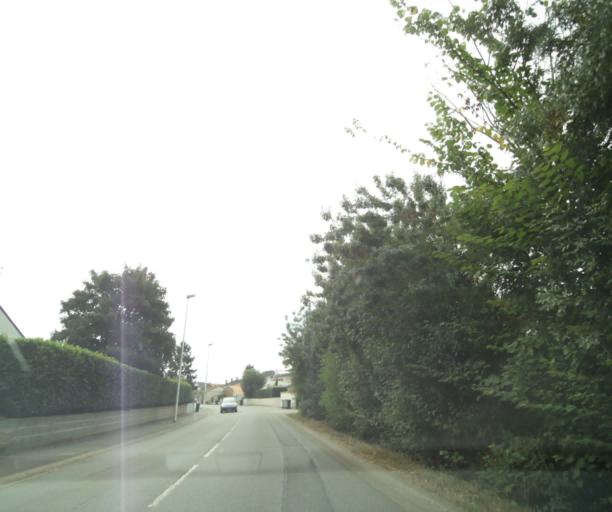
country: FR
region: Pays de la Loire
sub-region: Departement de la Loire-Atlantique
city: Saint-Herblain
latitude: 47.2072
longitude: -1.6359
